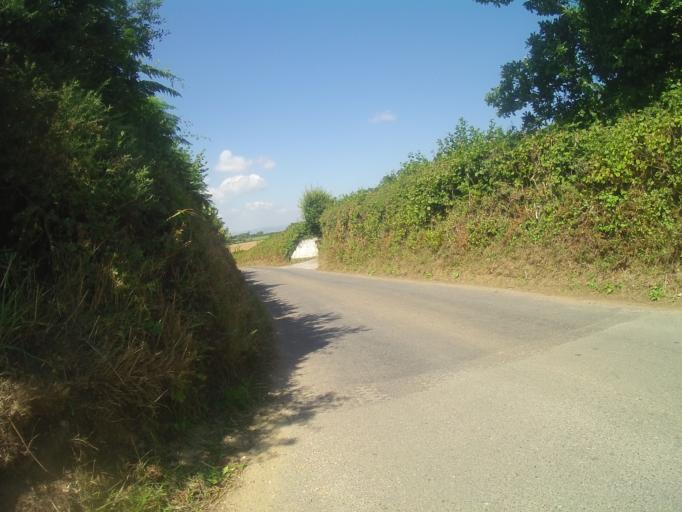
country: GB
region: England
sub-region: Devon
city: Dartmouth
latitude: 50.3640
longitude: -3.6283
